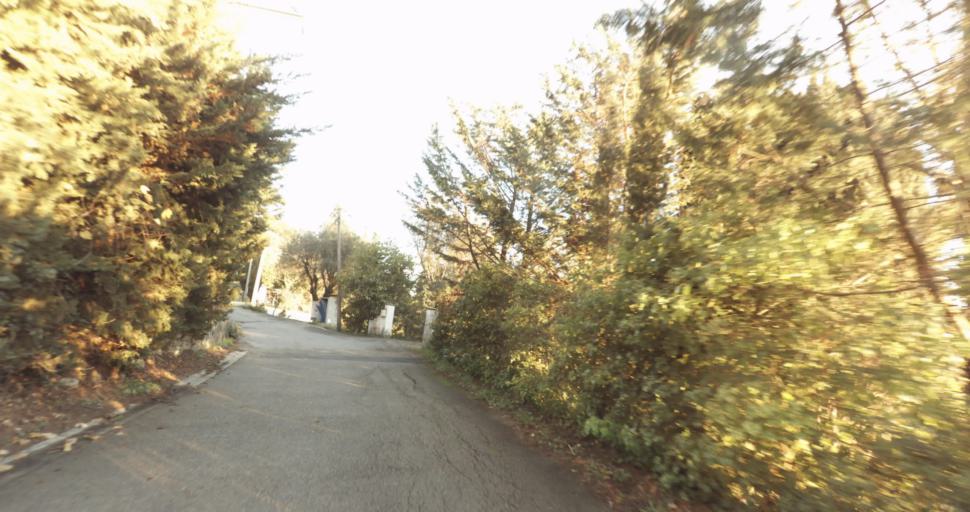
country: FR
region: Provence-Alpes-Cote d'Azur
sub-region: Departement des Alpes-Maritimes
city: Vence
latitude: 43.7296
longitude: 7.0949
